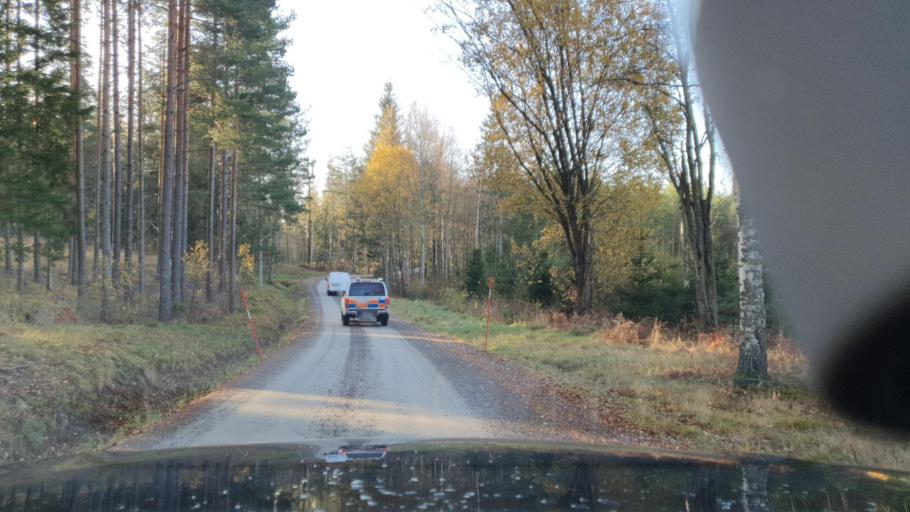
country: SE
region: Vaermland
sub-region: Grums Kommun
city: Grums
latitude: 59.4687
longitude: 12.9230
